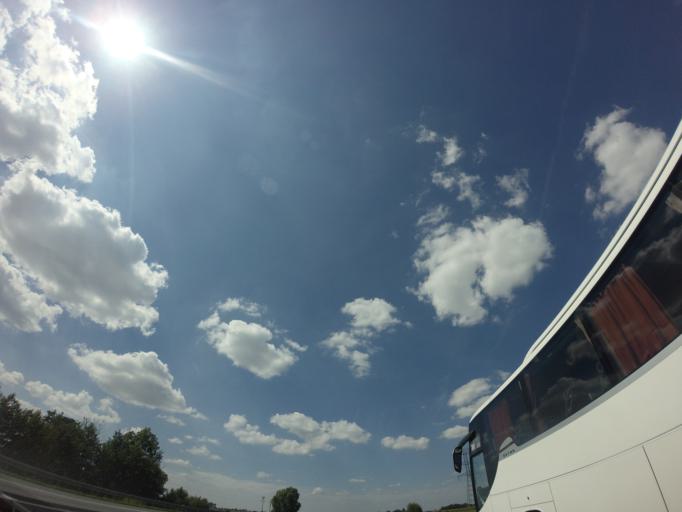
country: PL
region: Lower Silesian Voivodeship
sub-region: Powiat strzelinski
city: Wiazow
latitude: 50.8506
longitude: 17.2363
